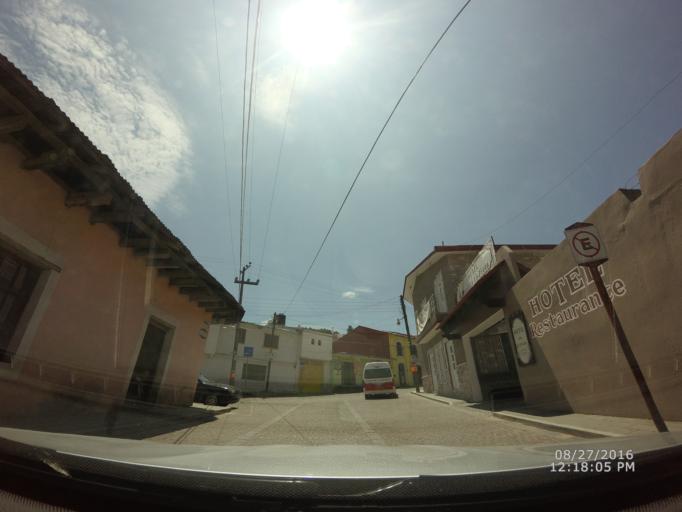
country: MX
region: Hidalgo
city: Mineral del Monte
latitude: 20.1384
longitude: -98.6712
